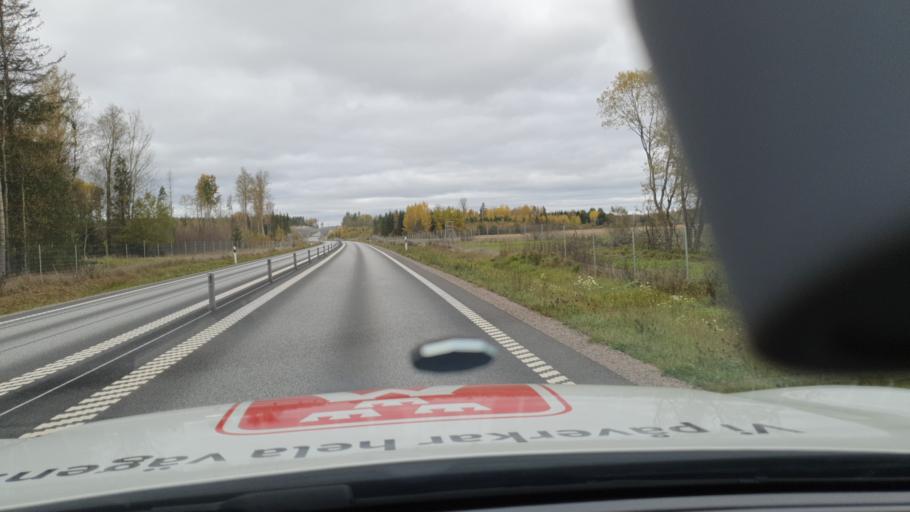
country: SE
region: OErebro
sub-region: Hallsbergs Kommun
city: Palsboda
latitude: 59.0435
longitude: 15.3462
